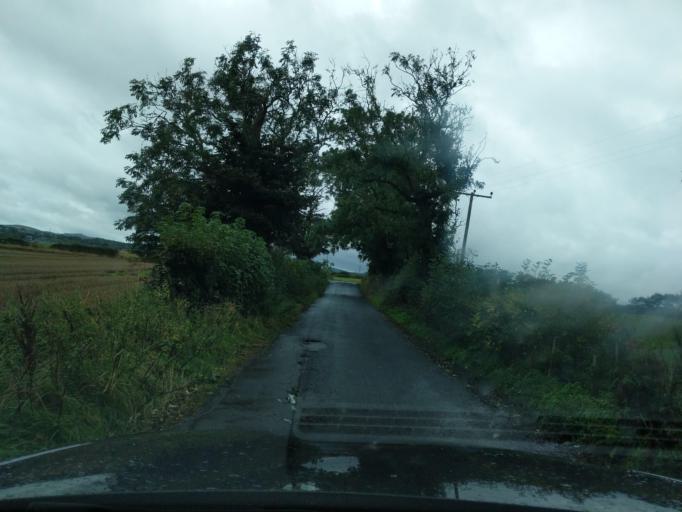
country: GB
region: Scotland
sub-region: Edinburgh
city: Balerno
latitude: 55.9043
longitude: -3.3399
